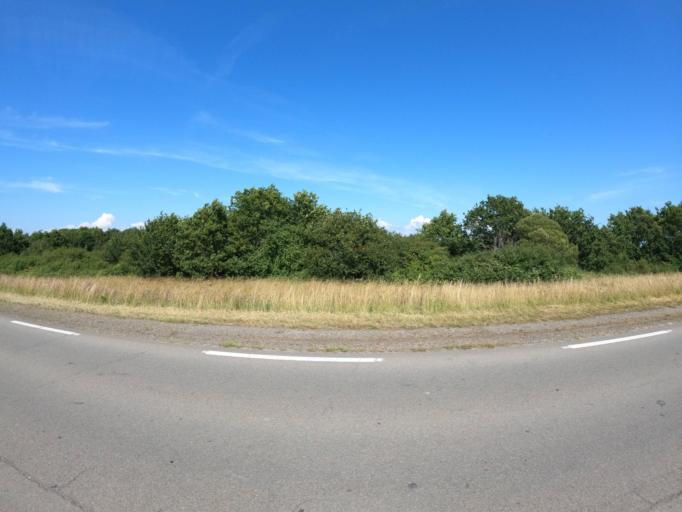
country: FR
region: Pays de la Loire
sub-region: Departement de la Loire-Atlantique
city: La Bernerie-en-Retz
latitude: 47.0993
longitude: -2.0379
